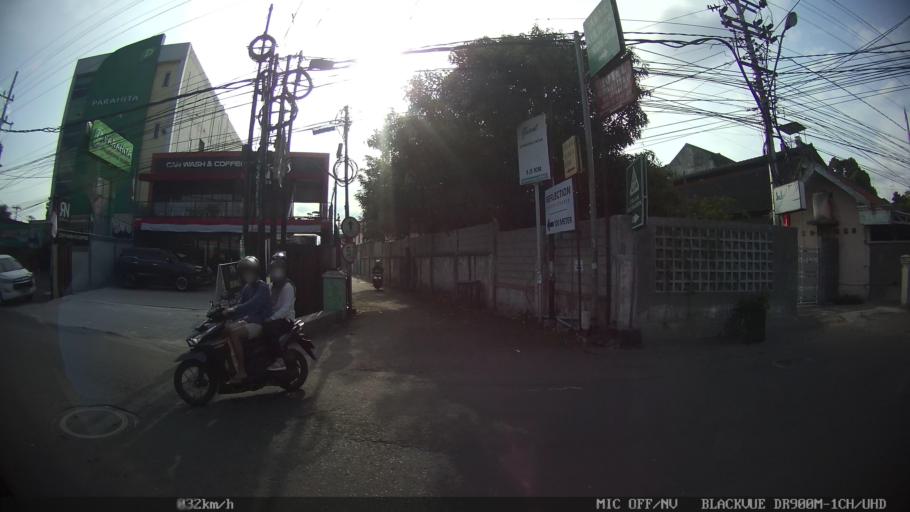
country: ID
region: Daerah Istimewa Yogyakarta
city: Melati
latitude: -7.7527
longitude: 110.3855
